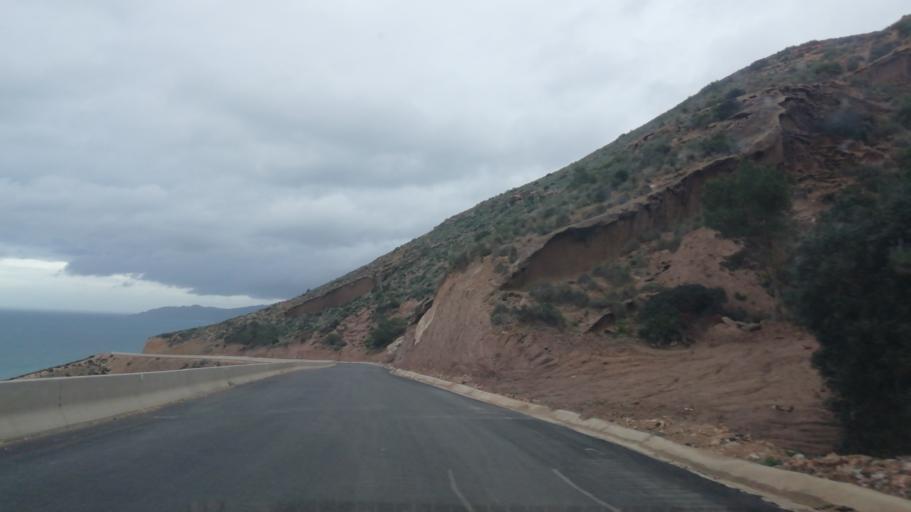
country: DZ
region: Oran
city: Bir el Djir
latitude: 35.7650
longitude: -0.5228
